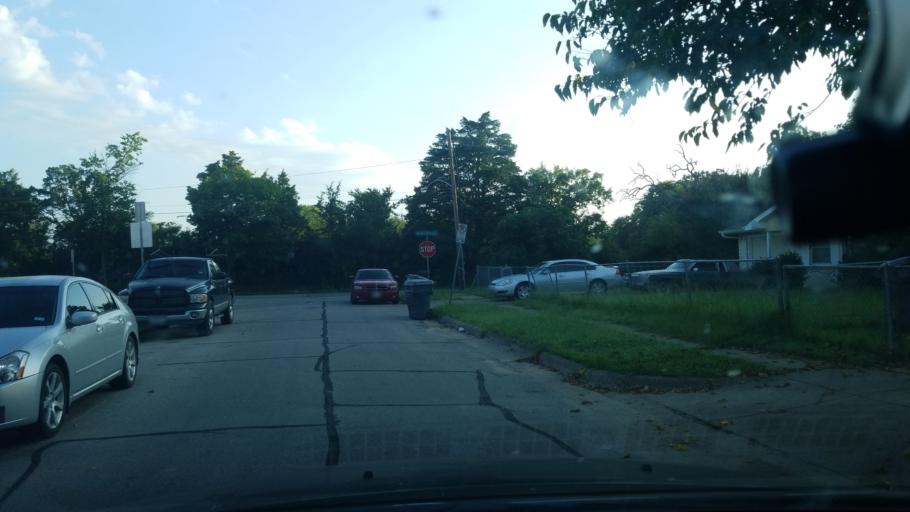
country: US
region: Texas
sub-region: Dallas County
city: Balch Springs
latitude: 32.7247
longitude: -96.6608
